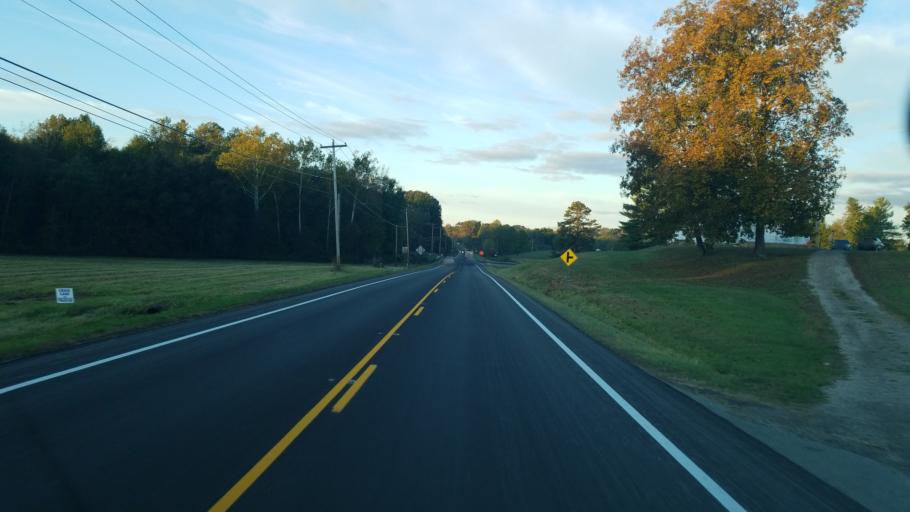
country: US
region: Ohio
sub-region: Vinton County
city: McArthur
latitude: 39.1988
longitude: -82.4944
